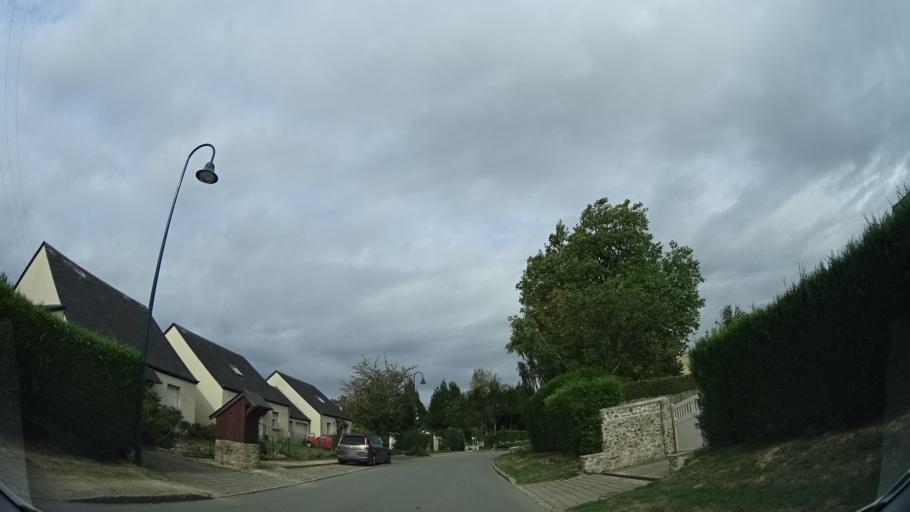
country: FR
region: Brittany
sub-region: Departement d'Ille-et-Vilaine
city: Hede-Bazouges
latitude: 48.2908
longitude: -1.8199
